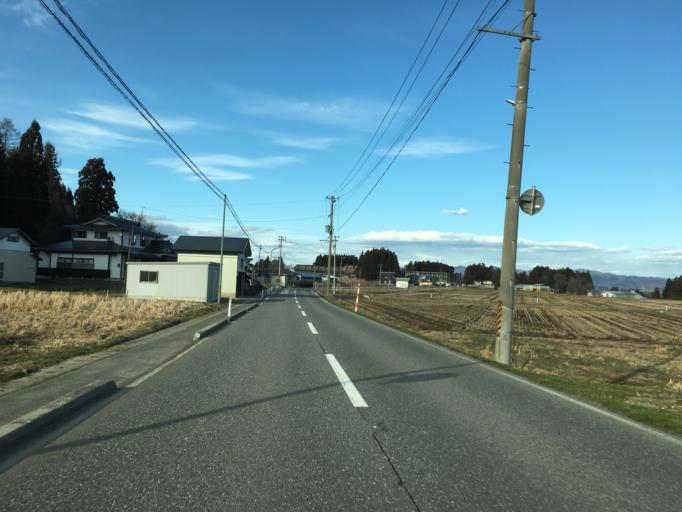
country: JP
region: Yamagata
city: Nagai
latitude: 38.0323
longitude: 139.9826
